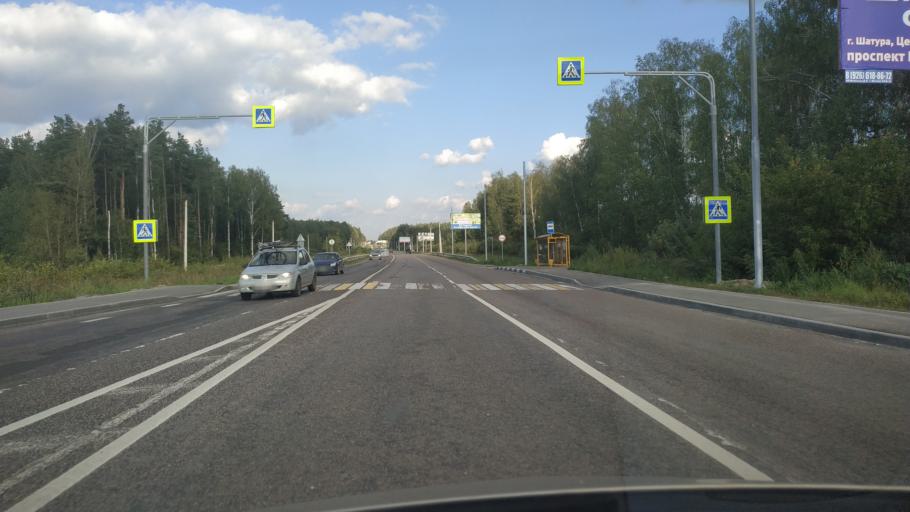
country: RU
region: Moskovskaya
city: Shaturtorf
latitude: 55.5776
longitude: 39.4238
